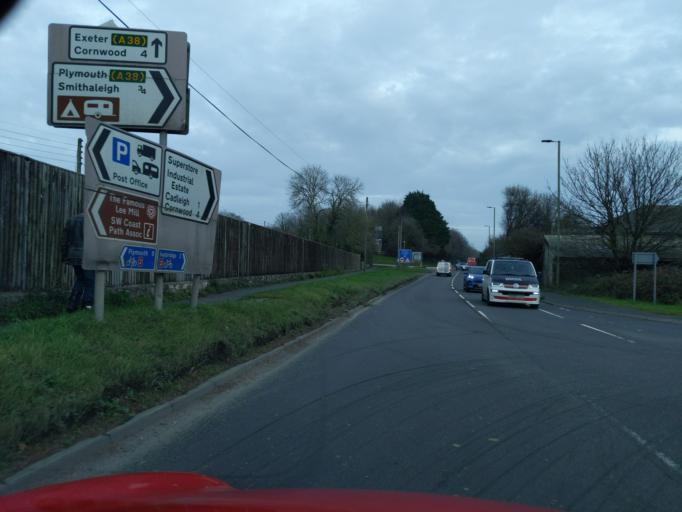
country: GB
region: England
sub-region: Devon
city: Yealmpton
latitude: 50.3851
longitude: -3.9692
